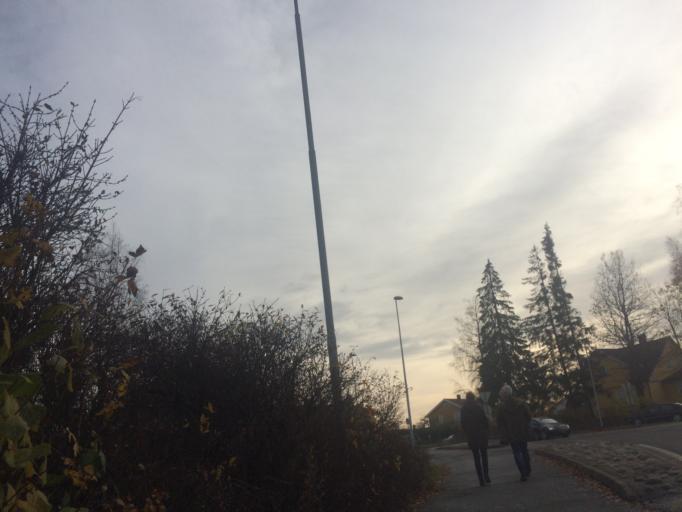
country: NO
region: Akershus
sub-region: Ski
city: Ski
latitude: 59.7220
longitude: 10.8464
